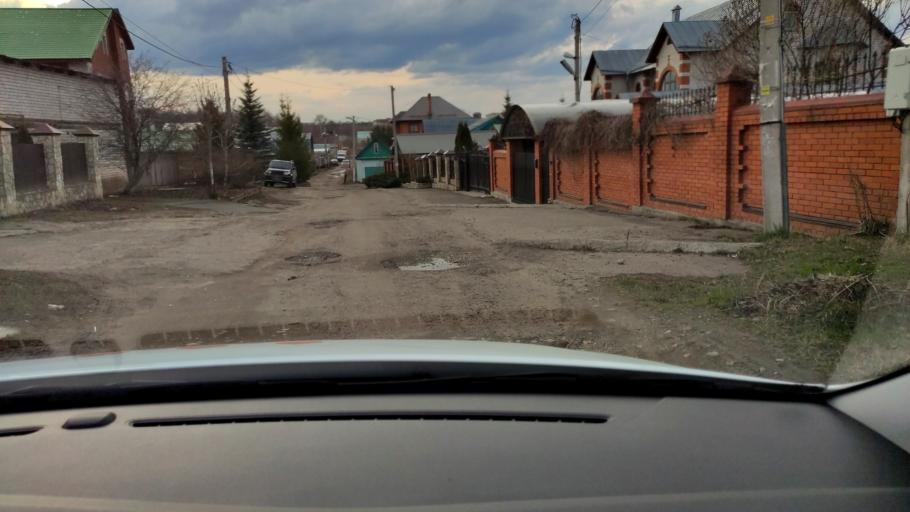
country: RU
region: Tatarstan
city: Stolbishchi
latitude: 55.7416
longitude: 49.2652
